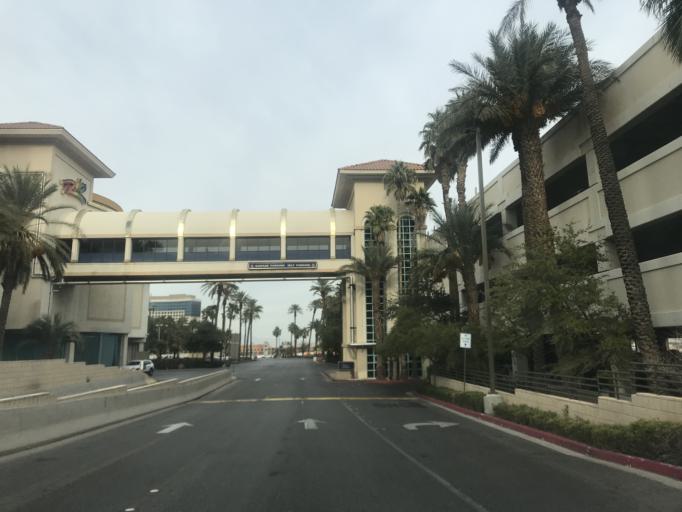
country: US
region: Nevada
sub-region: Clark County
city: Paradise
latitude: 36.1161
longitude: -115.1857
